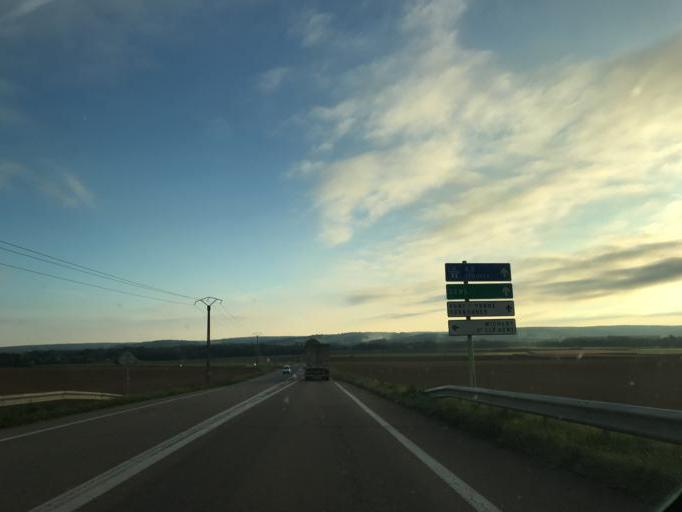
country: FR
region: Bourgogne
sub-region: Departement de l'Yonne
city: Sergines
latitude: 48.3245
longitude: 3.2262
